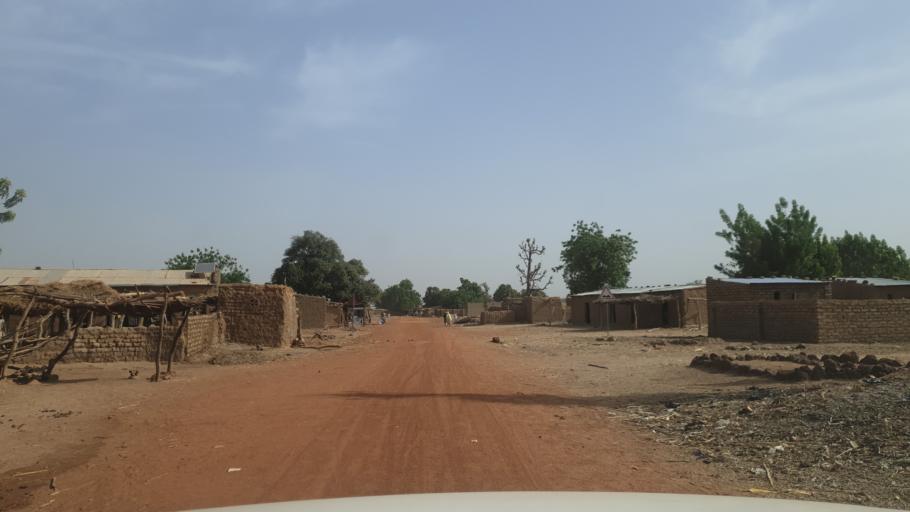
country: ML
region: Koulikoro
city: Kolokani
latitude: 13.3213
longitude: -8.2747
